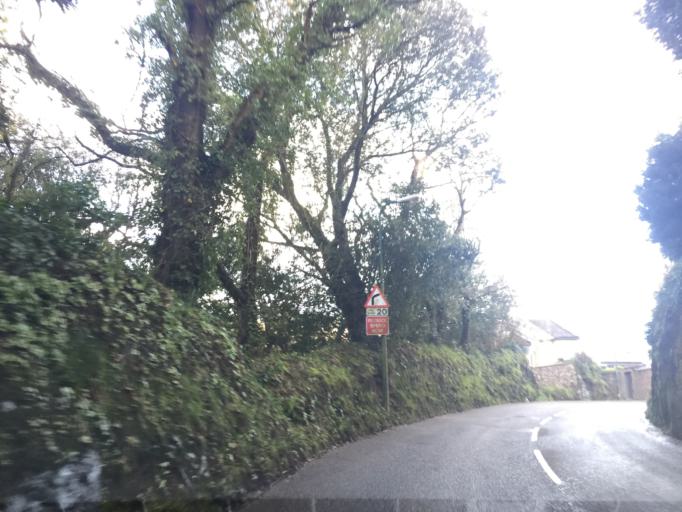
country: JE
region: St Helier
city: Saint Helier
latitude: 49.2010
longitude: -2.1373
